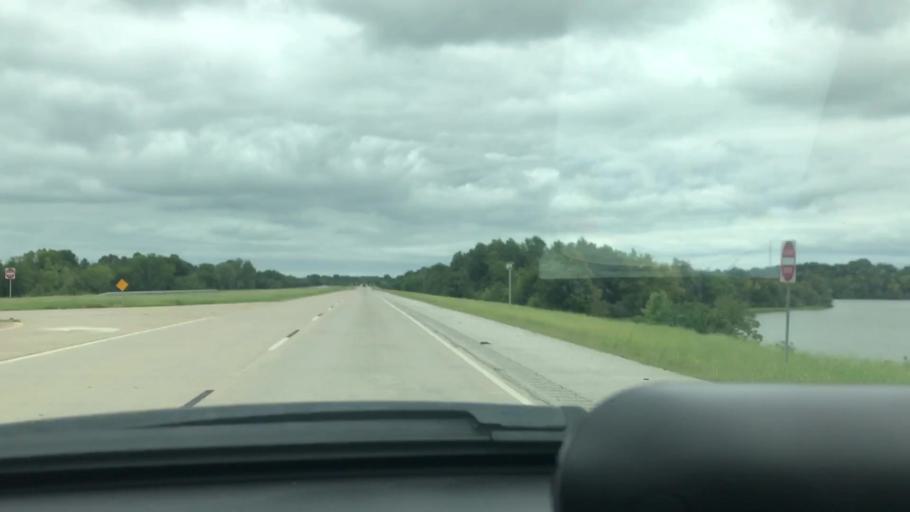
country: US
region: Oklahoma
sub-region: Wagoner County
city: Wagoner
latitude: 35.9001
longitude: -95.4026
